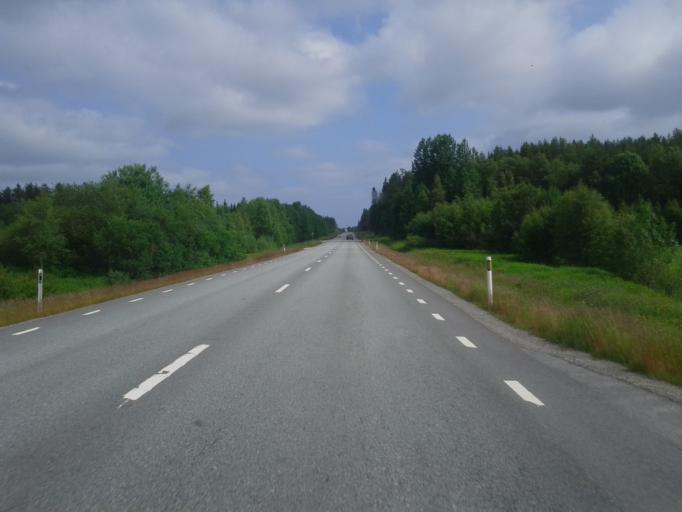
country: SE
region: Vaesterbotten
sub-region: Skelleftea Kommun
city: Burea
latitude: 64.3385
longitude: 21.2748
